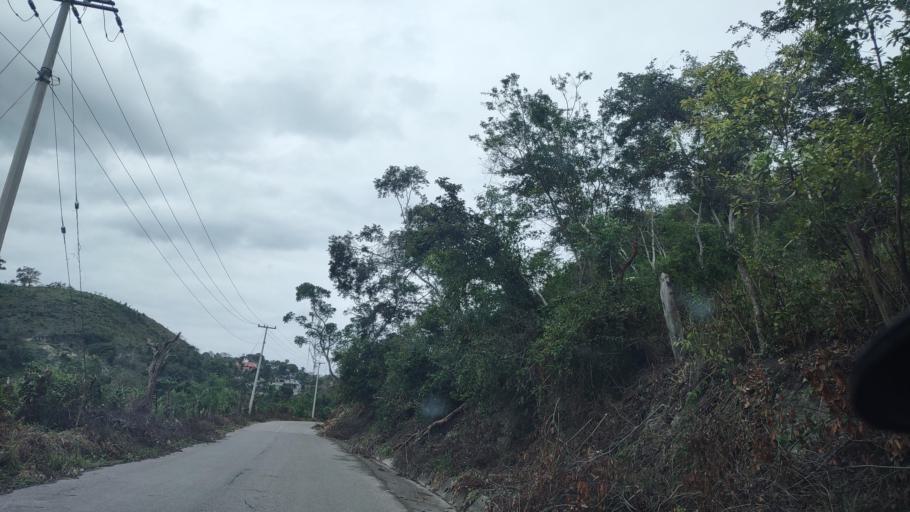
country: MX
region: Veracruz
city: Papantla de Olarte
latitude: 20.4424
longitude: -97.3008
